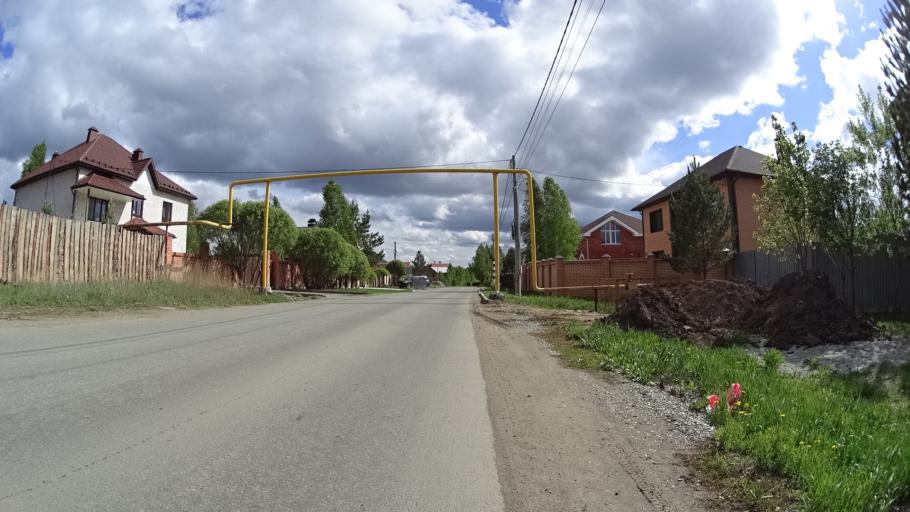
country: RU
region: Chelyabinsk
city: Sargazy
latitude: 55.1603
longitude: 61.2432
